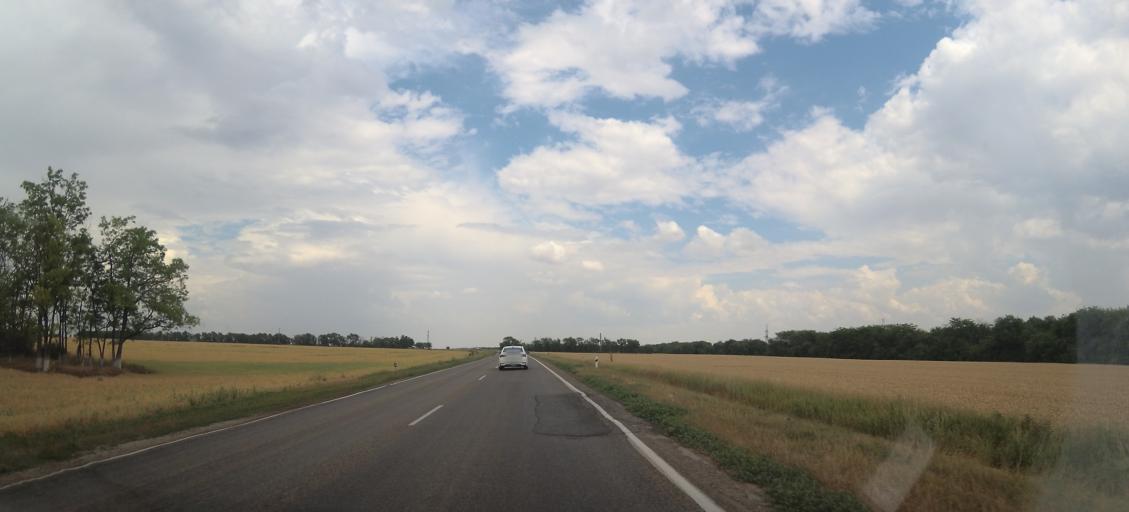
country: RU
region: Rostov
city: Peschanokopskoye
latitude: 46.2044
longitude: 41.2439
